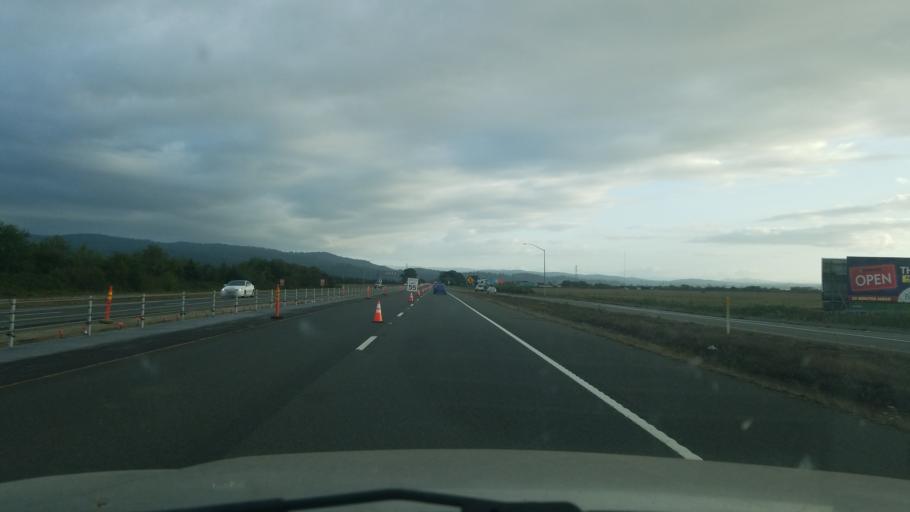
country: US
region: California
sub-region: Humboldt County
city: Arcata
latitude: 40.8602
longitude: -124.0838
